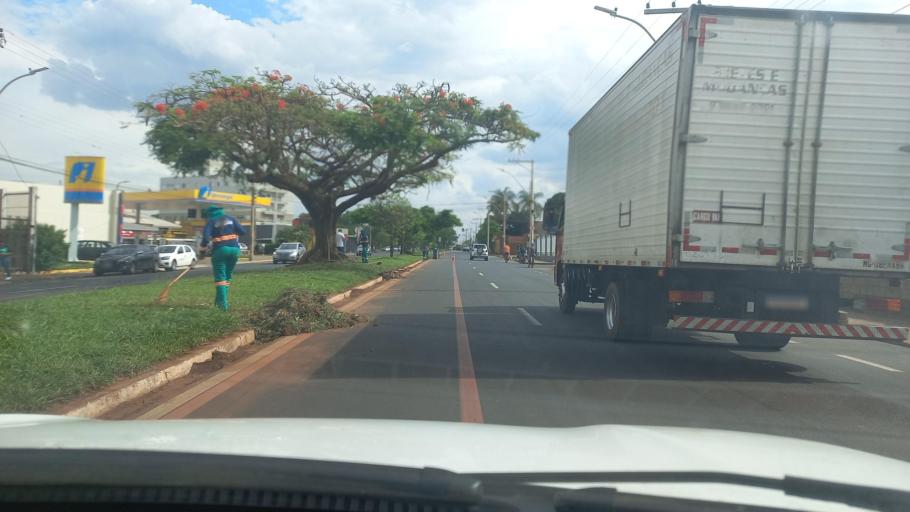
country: BR
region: Minas Gerais
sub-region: Uberaba
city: Uberaba
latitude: -19.7524
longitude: -47.9643
